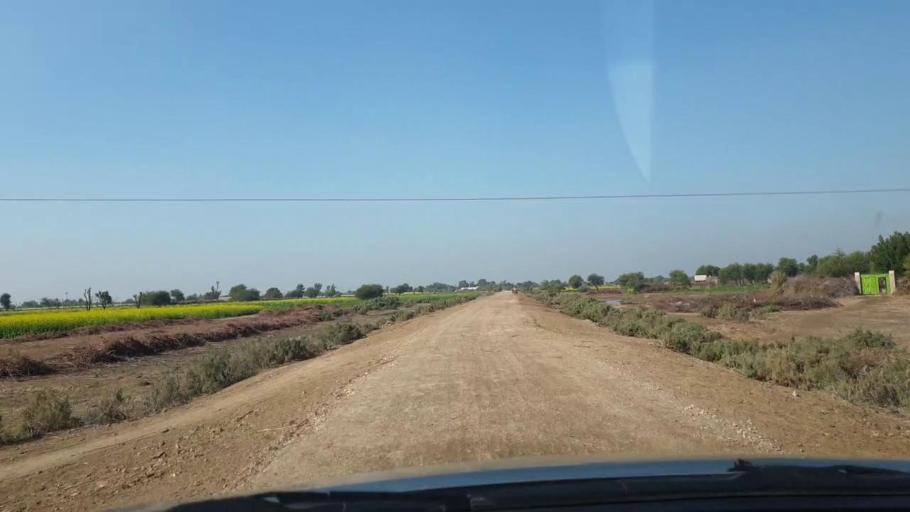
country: PK
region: Sindh
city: Jhol
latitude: 25.8808
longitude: 68.9086
